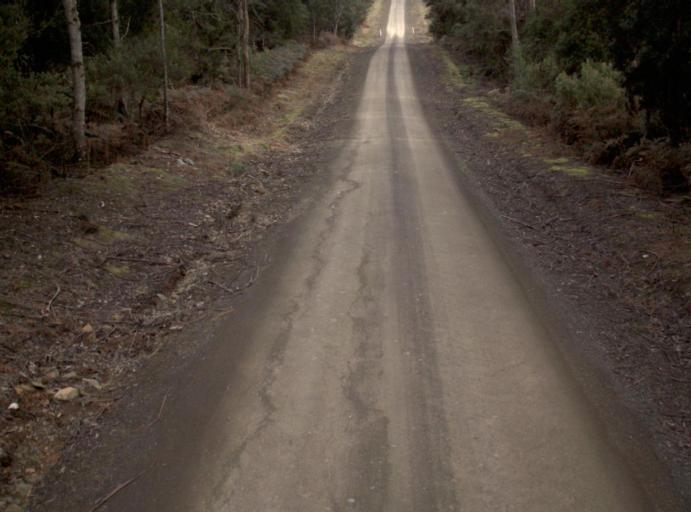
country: AU
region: Tasmania
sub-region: Dorset
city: Scottsdale
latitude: -41.2766
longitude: 147.3425
